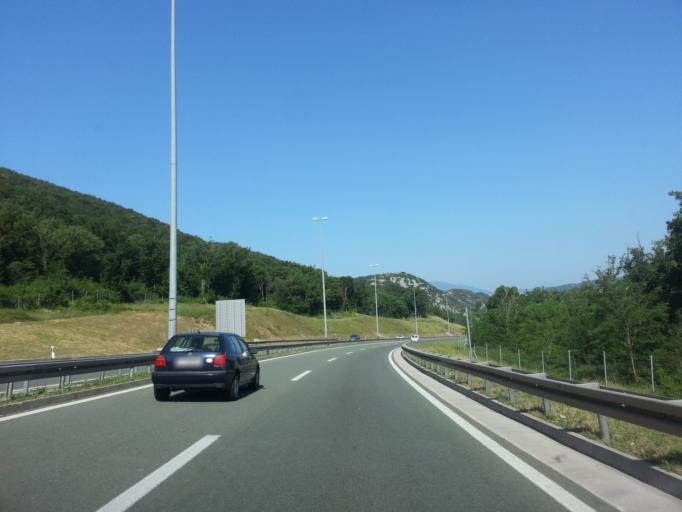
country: HR
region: Primorsko-Goranska
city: Skrljevo
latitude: 45.3144
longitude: 14.5143
